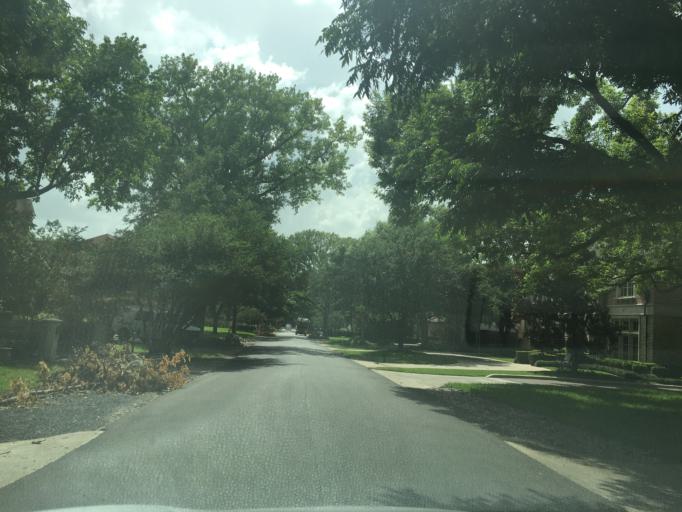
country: US
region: Texas
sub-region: Dallas County
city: University Park
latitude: 32.8843
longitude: -96.8010
